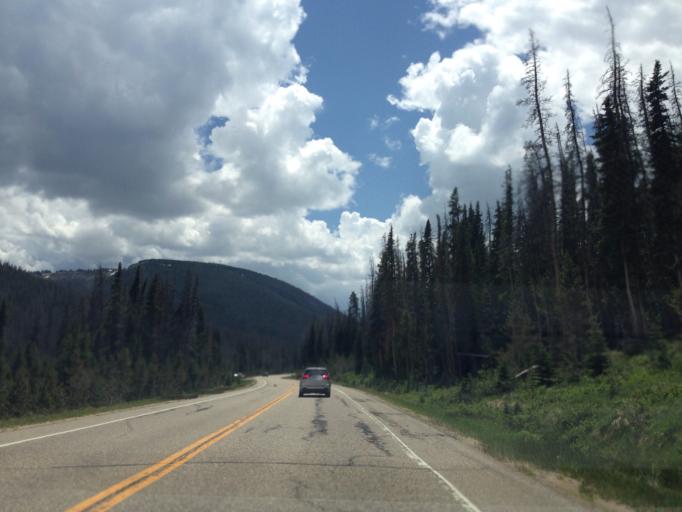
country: US
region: Colorado
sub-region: Larimer County
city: Estes Park
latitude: 40.5471
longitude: -105.8791
